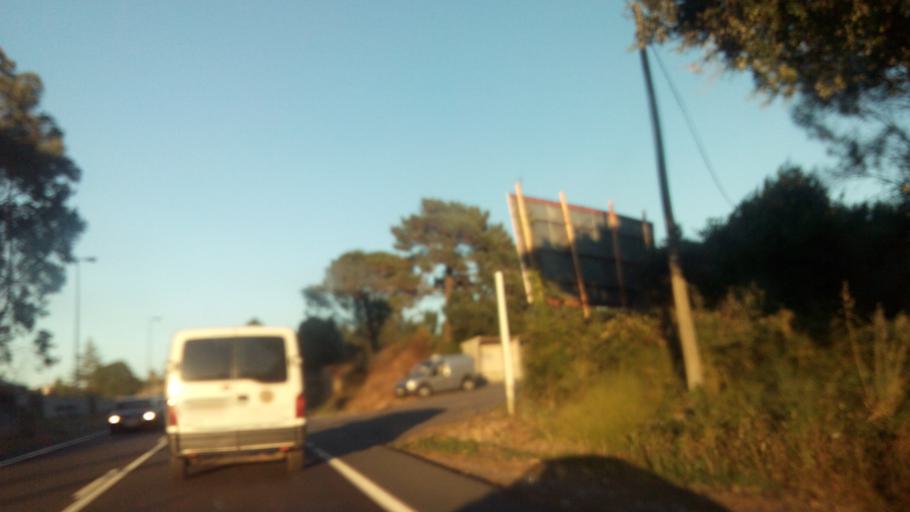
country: ES
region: Galicia
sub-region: Provincia de Pontevedra
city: Vilanova de Arousa
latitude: 42.5491
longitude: -8.8254
